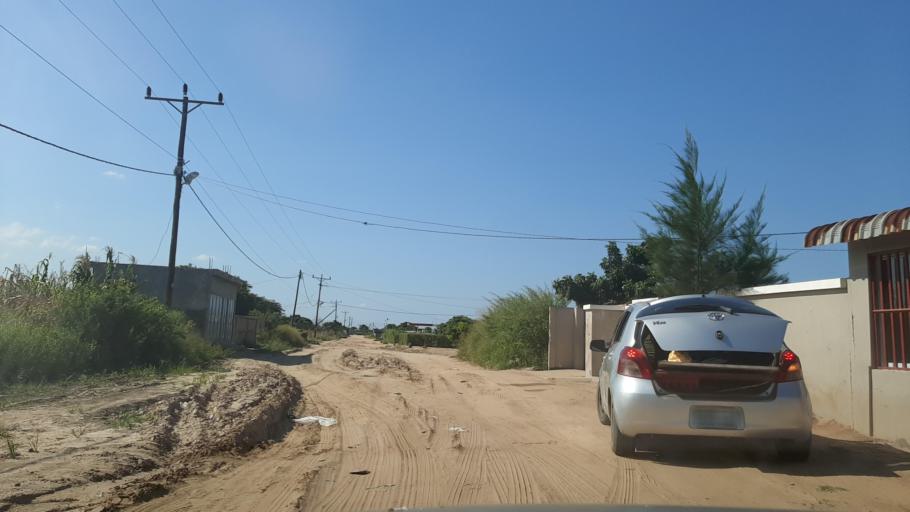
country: MZ
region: Maputo
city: Matola
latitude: -25.8144
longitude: 32.4916
